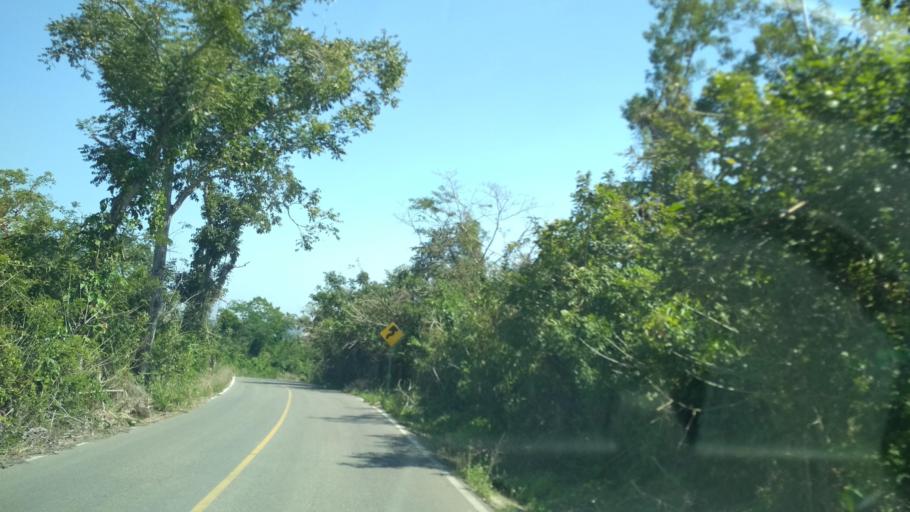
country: MX
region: Veracruz
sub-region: Papantla
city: Polutla
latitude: 20.4683
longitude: -97.2246
